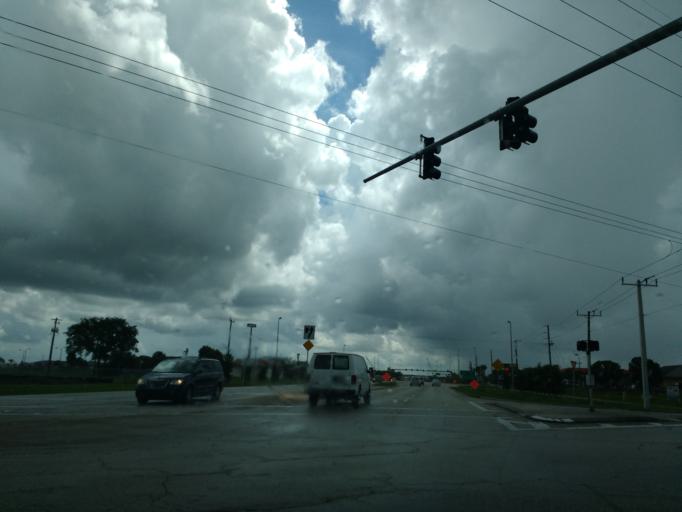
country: US
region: Florida
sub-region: Charlotte County
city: Charlotte Park
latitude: 26.8949
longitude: -82.0113
